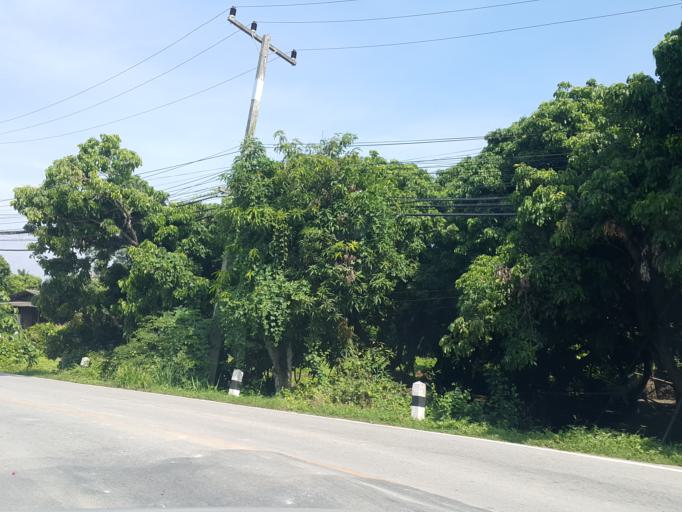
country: TH
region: Chiang Mai
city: Saraphi
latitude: 18.6903
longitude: 99.0599
